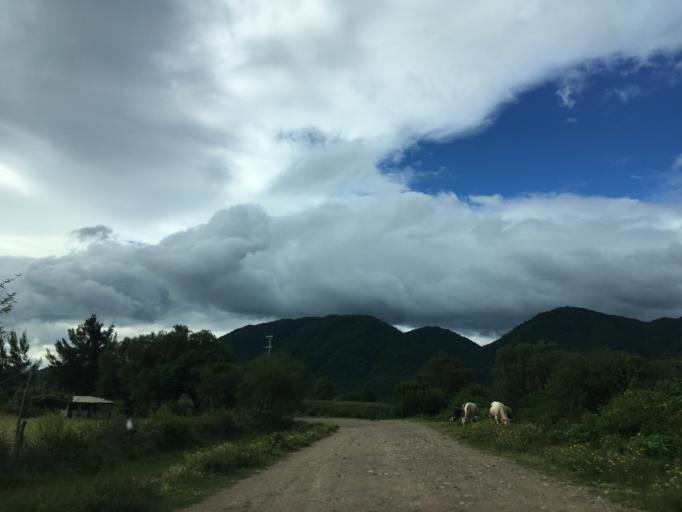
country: MX
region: Guanajuato
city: Iramuco
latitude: 19.9698
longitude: -100.9481
